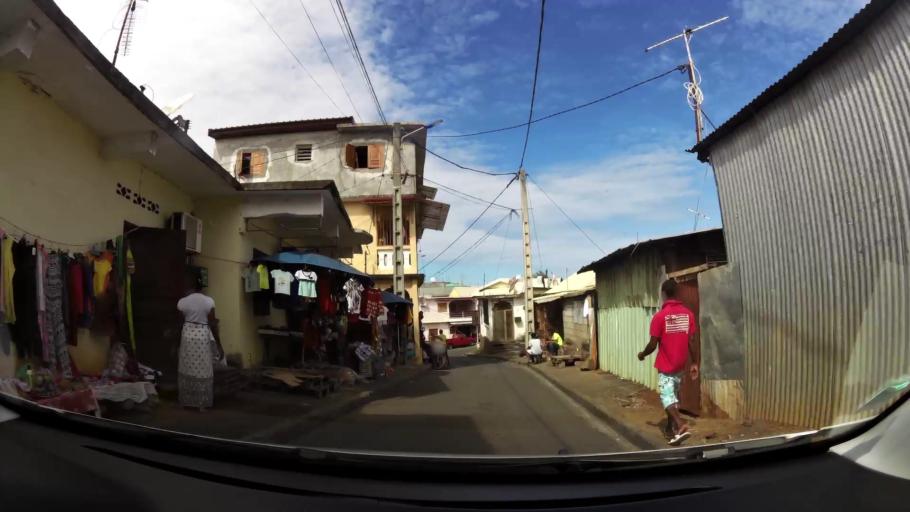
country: YT
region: Mamoudzou
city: Mamoudzou
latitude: -12.7803
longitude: 45.2293
